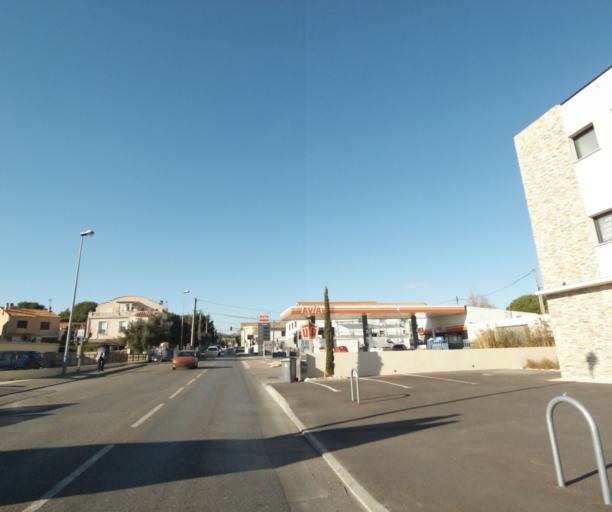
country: FR
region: Provence-Alpes-Cote d'Azur
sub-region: Departement des Bouches-du-Rhone
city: La Ciotat
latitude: 43.1848
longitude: 5.6088
